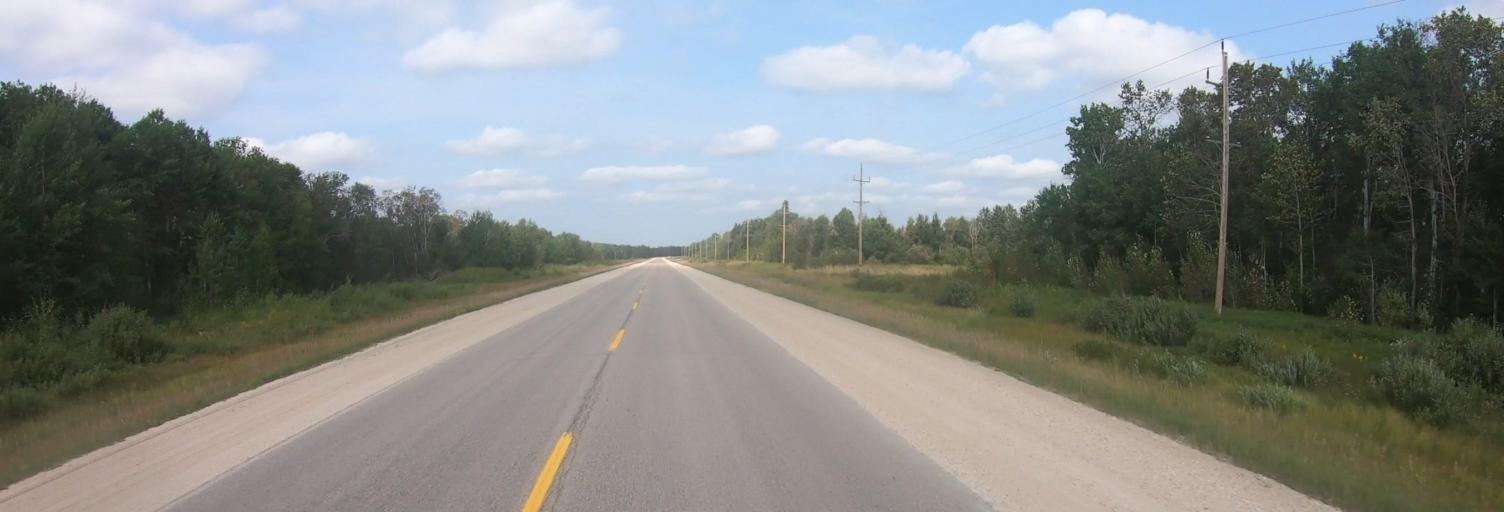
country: CA
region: Manitoba
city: La Broquerie
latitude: 49.2323
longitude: -96.3330
